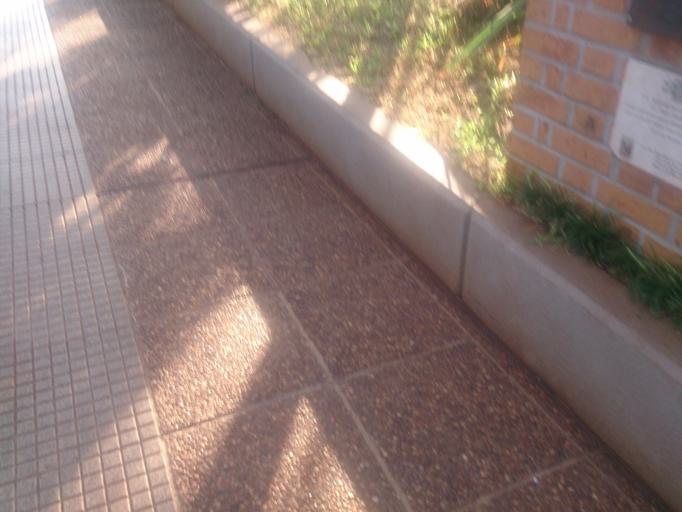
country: AR
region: Misiones
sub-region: Departamento de Obera
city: Obera
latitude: -27.4852
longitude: -55.1209
